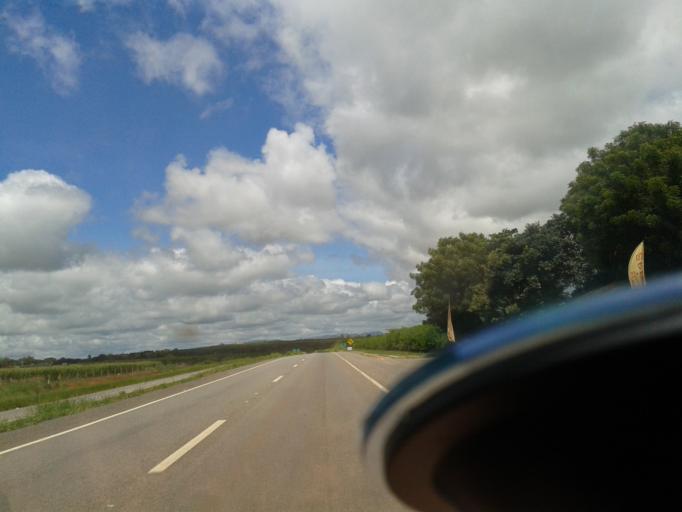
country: BR
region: Goias
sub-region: Itaberai
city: Itaberai
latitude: -16.0728
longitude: -49.7548
